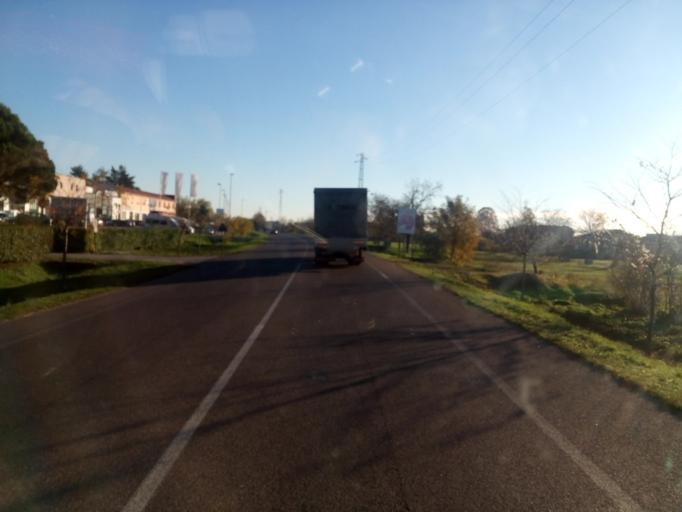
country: IT
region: Veneto
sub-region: Provincia di Vicenza
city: Sarcedo
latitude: 45.6924
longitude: 11.5288
